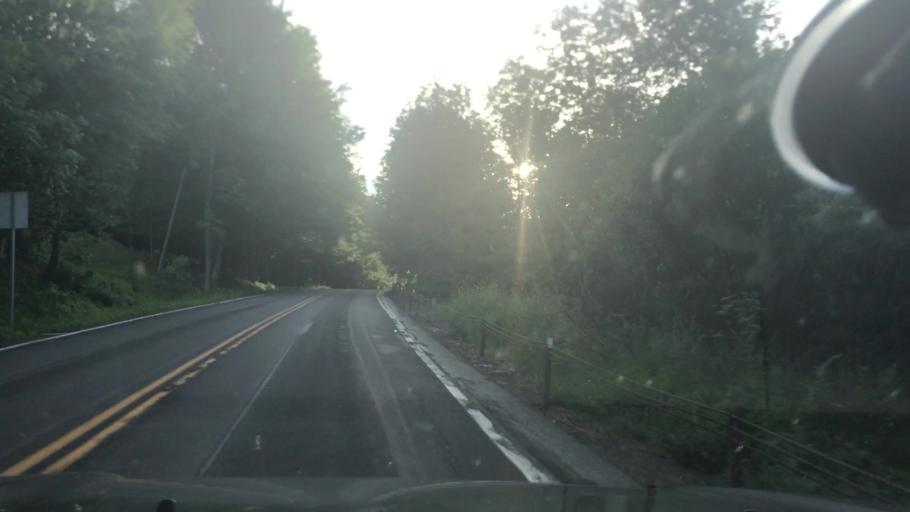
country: US
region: New York
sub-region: Otsego County
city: Unadilla
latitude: 42.3386
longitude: -75.2498
